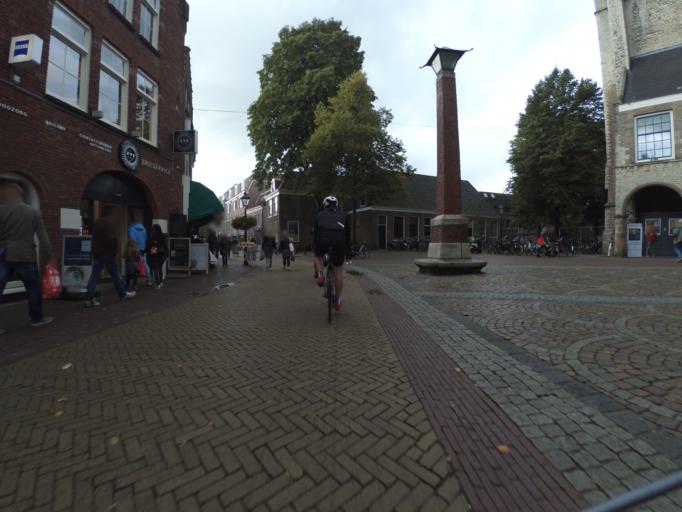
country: NL
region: North Holland
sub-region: Gemeente Alkmaar
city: Alkmaar
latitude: 52.6323
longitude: 4.7444
